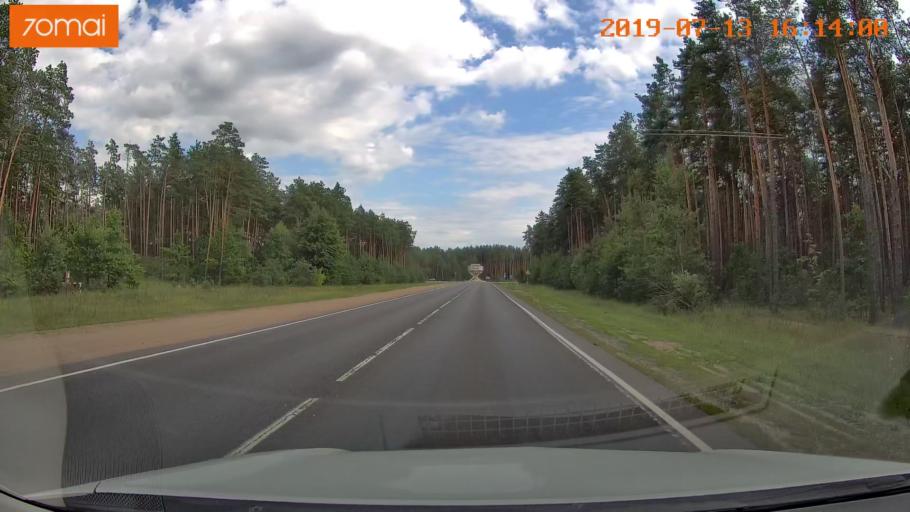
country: BY
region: Mogilev
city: Babruysk
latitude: 53.1585
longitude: 29.3141
